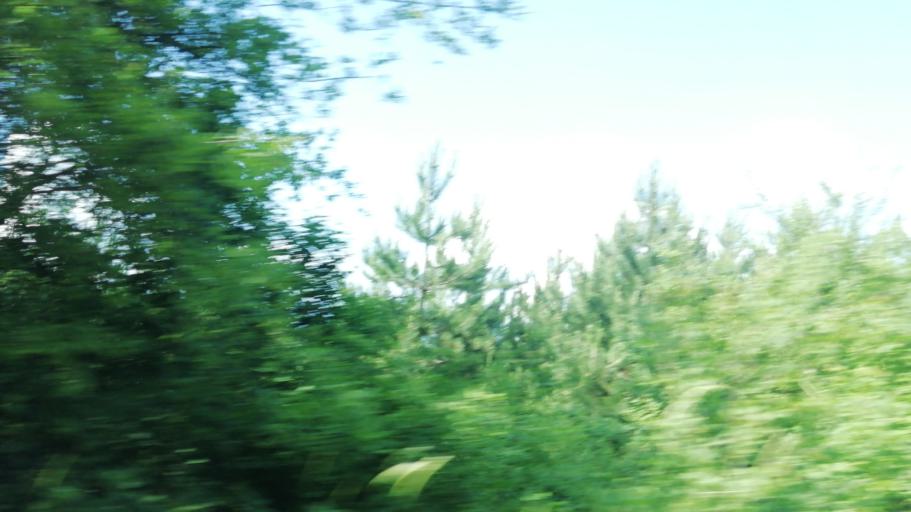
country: TR
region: Karabuk
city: Karabuk
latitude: 41.1247
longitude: 32.5884
